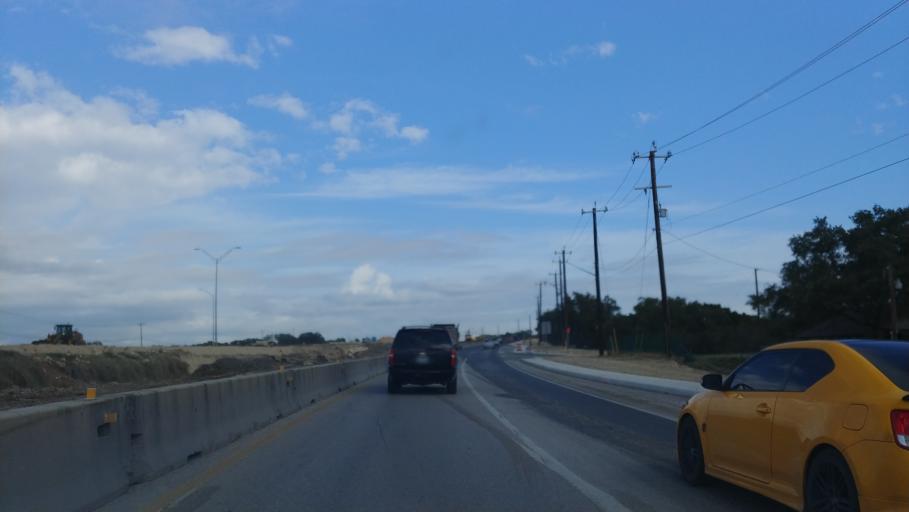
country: US
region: Texas
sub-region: Bexar County
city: Leon Valley
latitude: 29.4515
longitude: -98.7110
